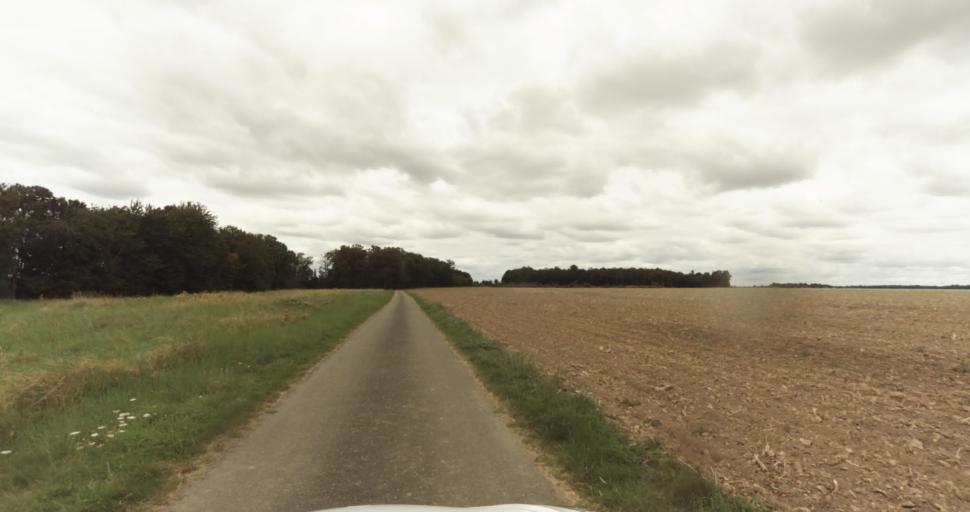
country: FR
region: Haute-Normandie
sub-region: Departement de l'Eure
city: Nonancourt
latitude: 48.8144
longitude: 1.1654
